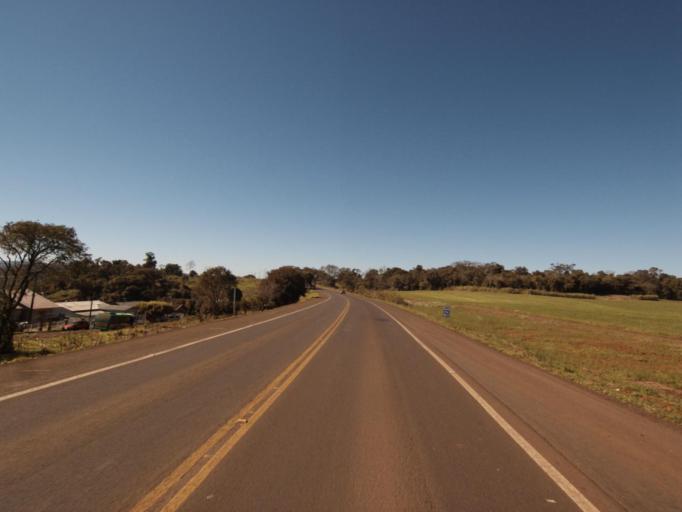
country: BR
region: Santa Catarina
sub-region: Chapeco
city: Chapeco
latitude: -26.9054
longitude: -52.8993
